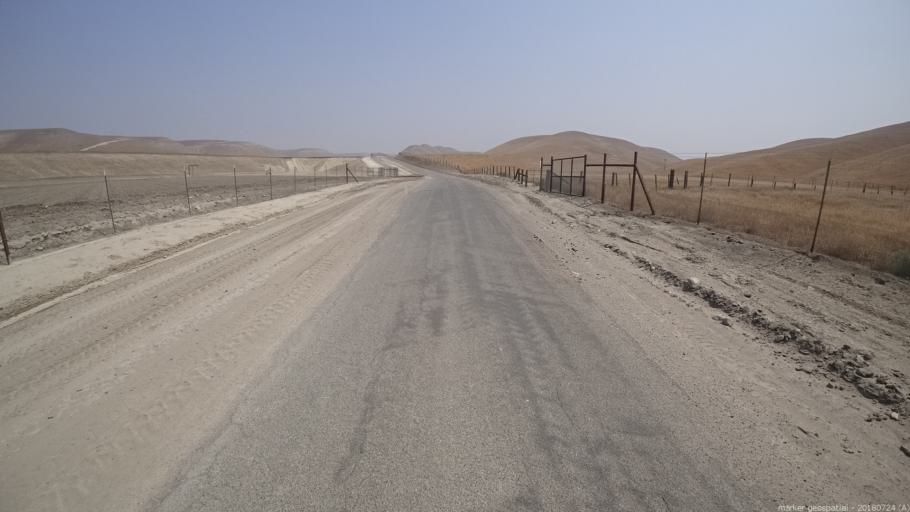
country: US
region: California
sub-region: Monterey County
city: King City
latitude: 36.1981
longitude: -121.0288
